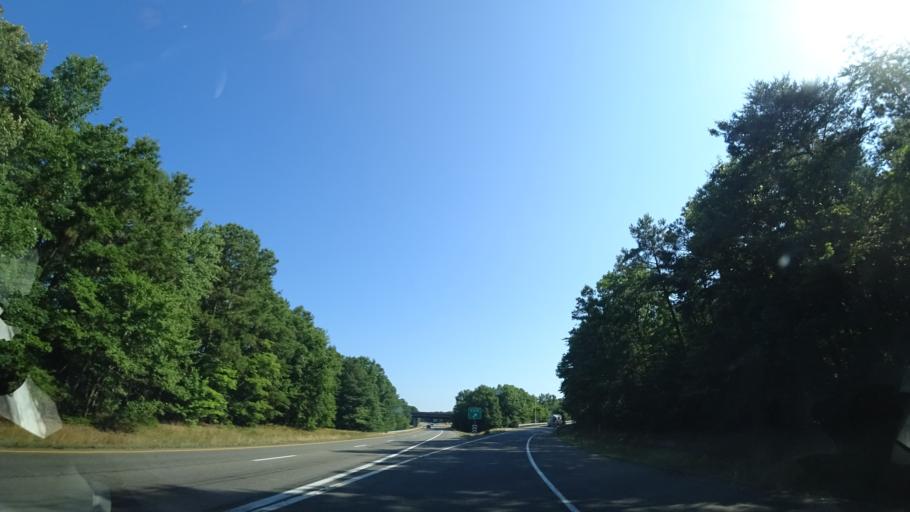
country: US
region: Virginia
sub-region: Henrico County
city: Sandston
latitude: 37.5160
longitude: -77.2704
